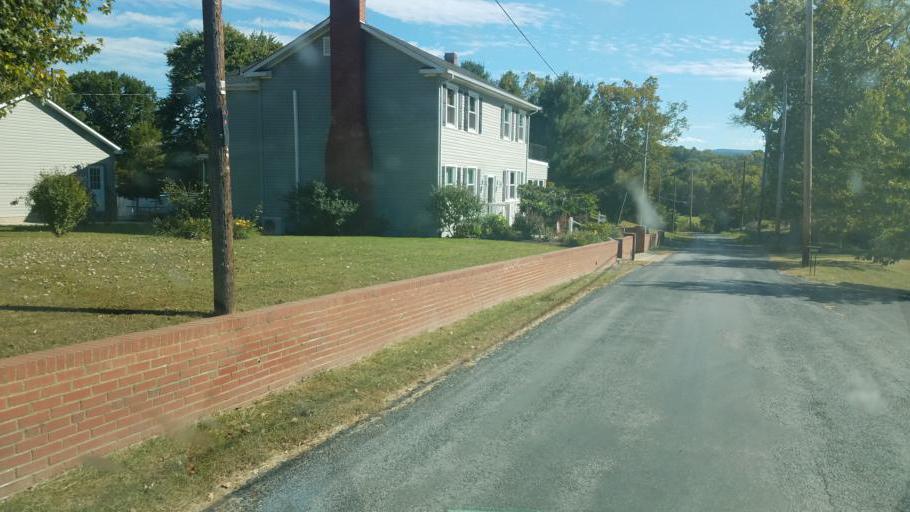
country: US
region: Virginia
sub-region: Warren County
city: Front Royal
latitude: 38.9461
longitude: -78.1961
